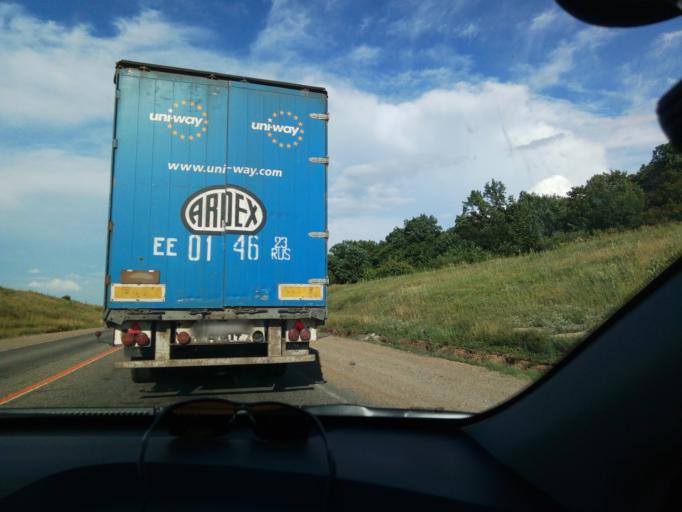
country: RU
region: Adygeya
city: Kuzhorskaya
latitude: 44.6474
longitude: 40.3063
